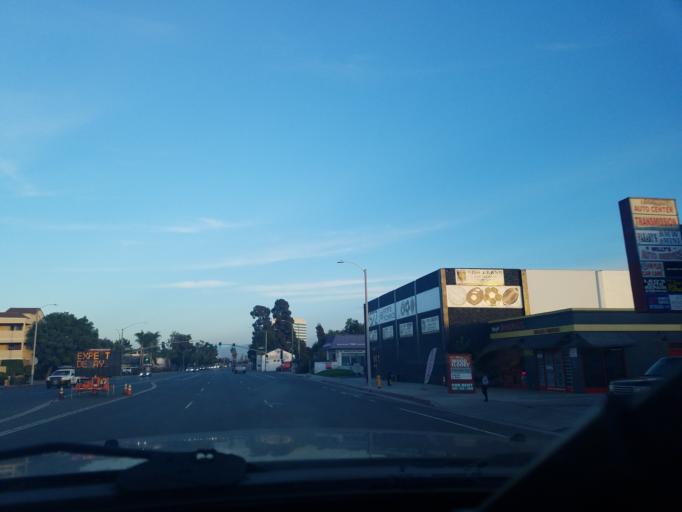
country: US
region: California
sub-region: Orange County
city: Midway City
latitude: 33.7156
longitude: -117.9973
